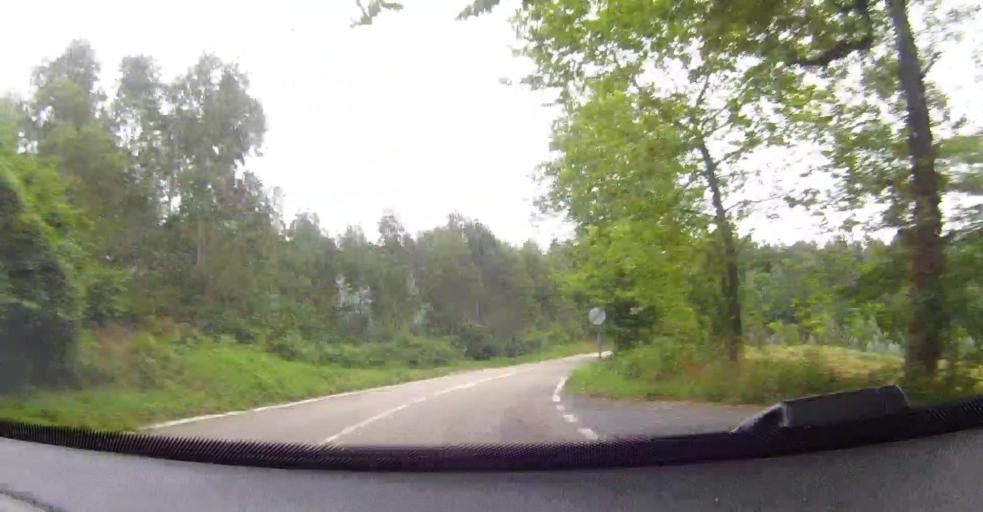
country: ES
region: Basque Country
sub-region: Bizkaia
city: Balmaseda
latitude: 43.2394
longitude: -3.2870
